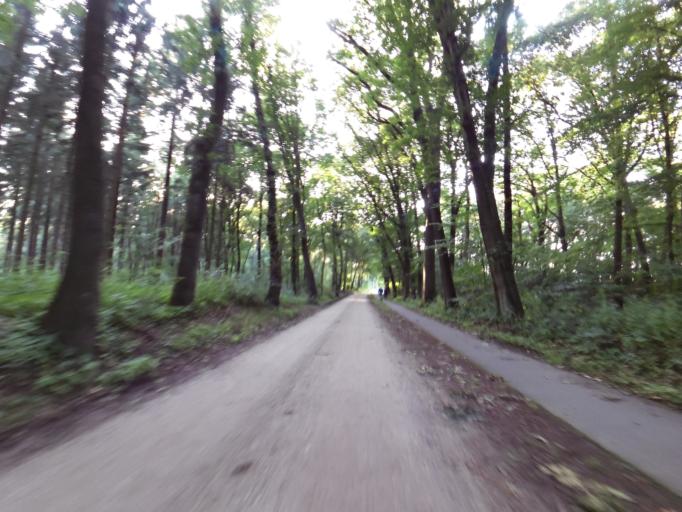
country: NL
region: Gelderland
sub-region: Gemeente Doetinchem
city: Doetinchem
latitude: 51.9917
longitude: 6.2760
